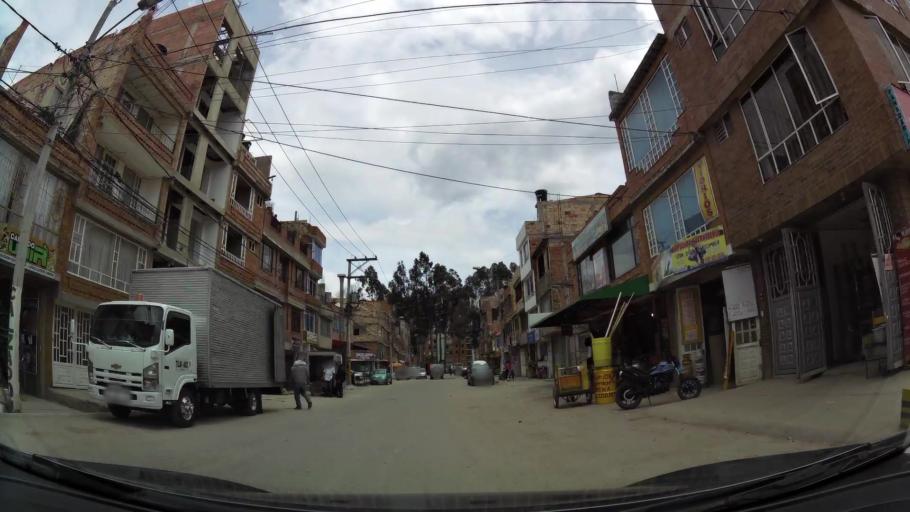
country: CO
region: Cundinamarca
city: Funza
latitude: 4.7194
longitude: -74.1312
